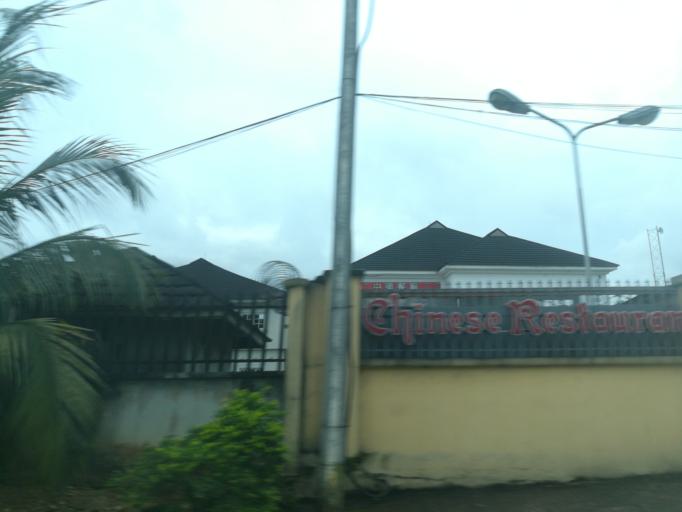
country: NG
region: Rivers
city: Port Harcourt
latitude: 4.8154
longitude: 7.0015
